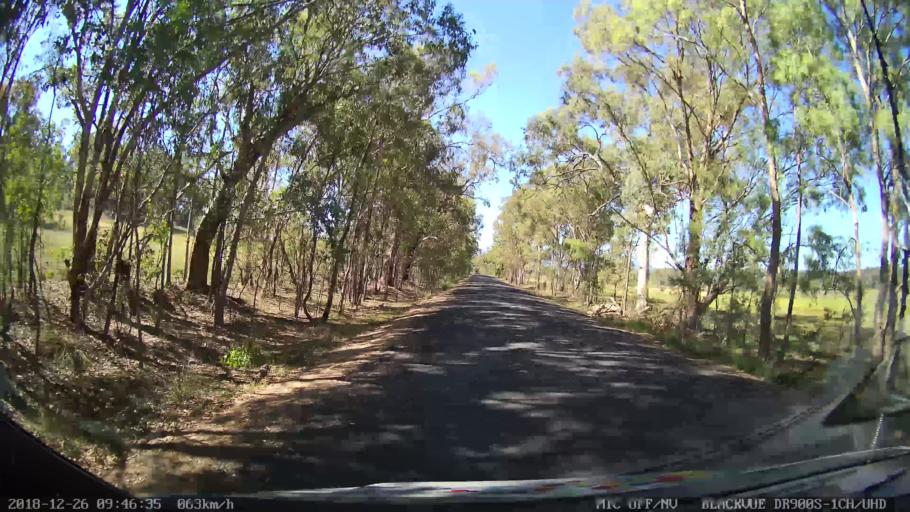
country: AU
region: New South Wales
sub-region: Mid-Western Regional
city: Kandos
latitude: -32.9711
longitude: 150.1050
